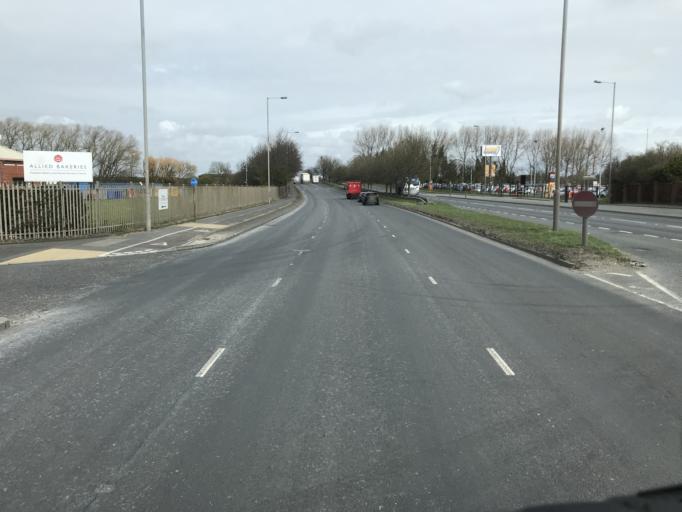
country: GB
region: England
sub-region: Sefton
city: Maghull
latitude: 53.4847
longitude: -2.9612
